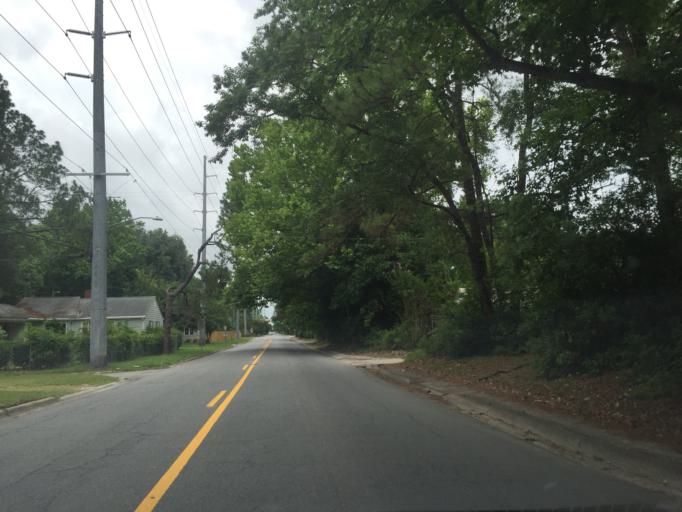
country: US
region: Georgia
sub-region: Chatham County
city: Thunderbolt
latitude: 32.0318
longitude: -81.1001
